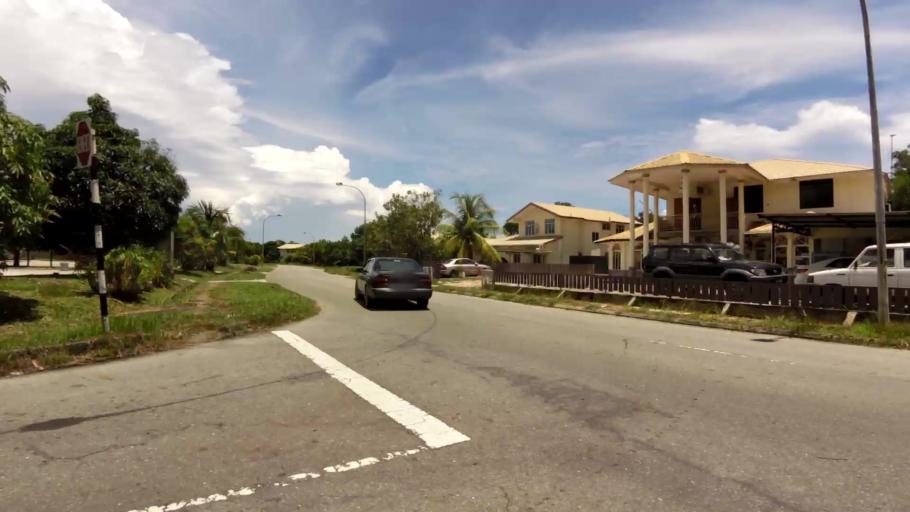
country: BN
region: Brunei and Muara
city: Bandar Seri Begawan
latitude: 4.9642
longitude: 114.9171
